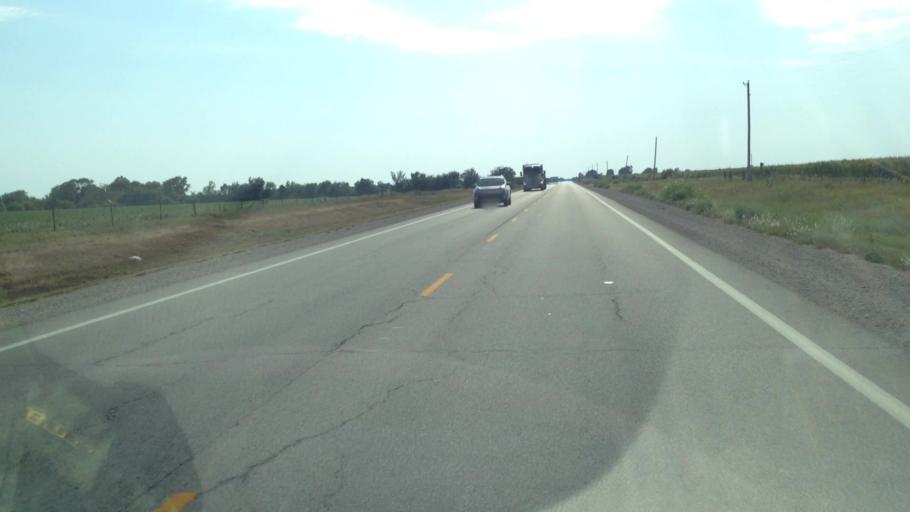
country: US
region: Kansas
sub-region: Anderson County
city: Garnett
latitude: 38.0816
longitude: -95.2103
